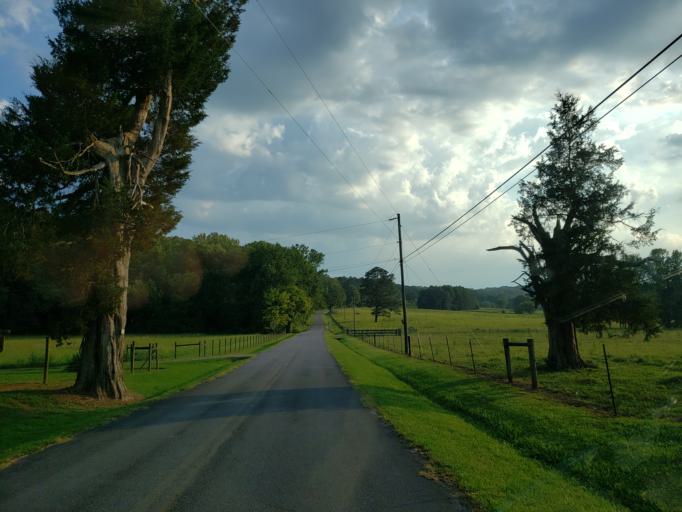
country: US
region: Georgia
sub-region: Polk County
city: Aragon
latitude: 34.0586
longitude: -84.9813
